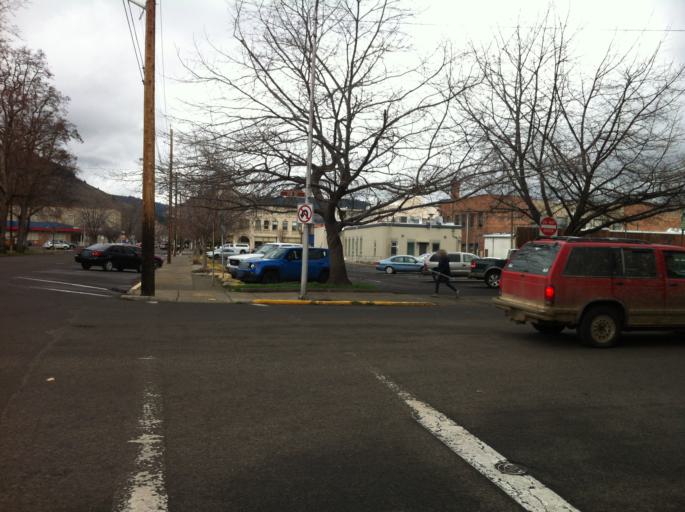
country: US
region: Oregon
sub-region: Union County
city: La Grande
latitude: 45.3267
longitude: -118.0930
